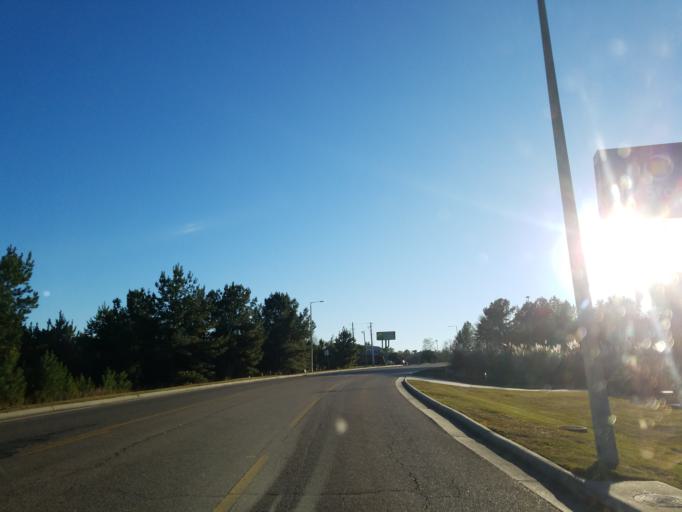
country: US
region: Mississippi
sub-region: Lamar County
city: Arnold Line
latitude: 31.3563
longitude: -89.3506
